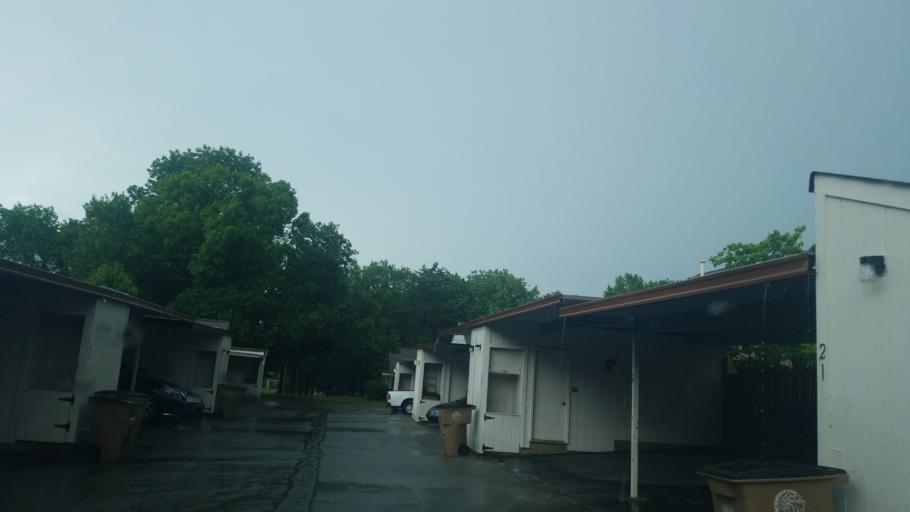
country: US
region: Tennessee
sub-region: Rutherford County
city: La Vergne
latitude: 36.1046
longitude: -86.6016
